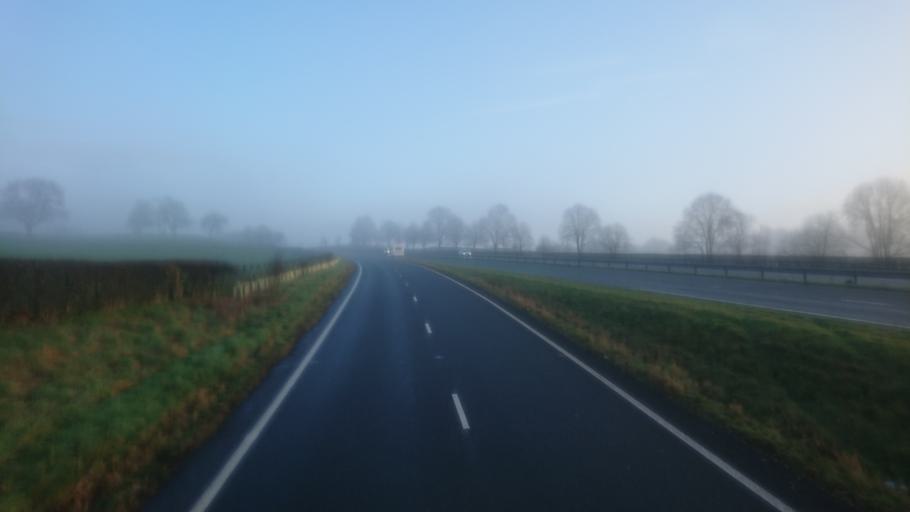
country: GB
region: England
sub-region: Cumbria
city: Milnthorpe
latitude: 54.2644
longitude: -2.7771
